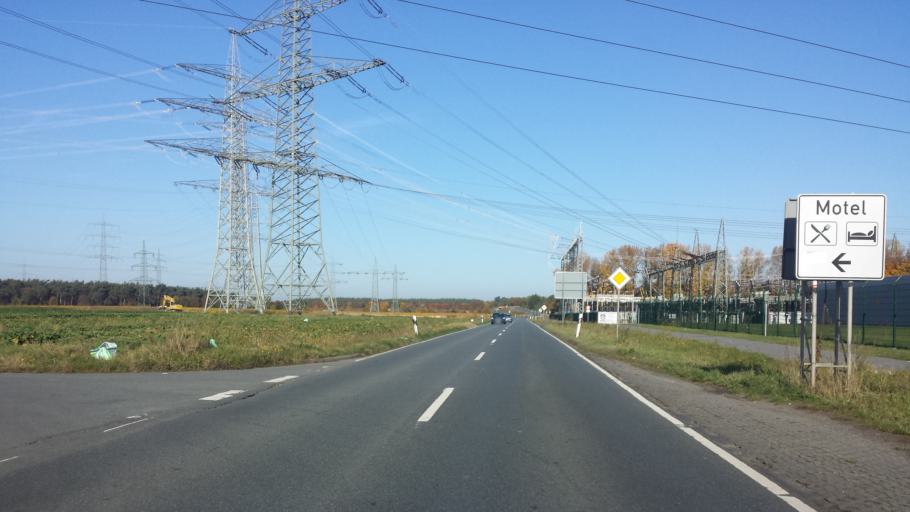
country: DE
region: Hesse
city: Pfungstadt
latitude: 49.8141
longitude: 8.5881
